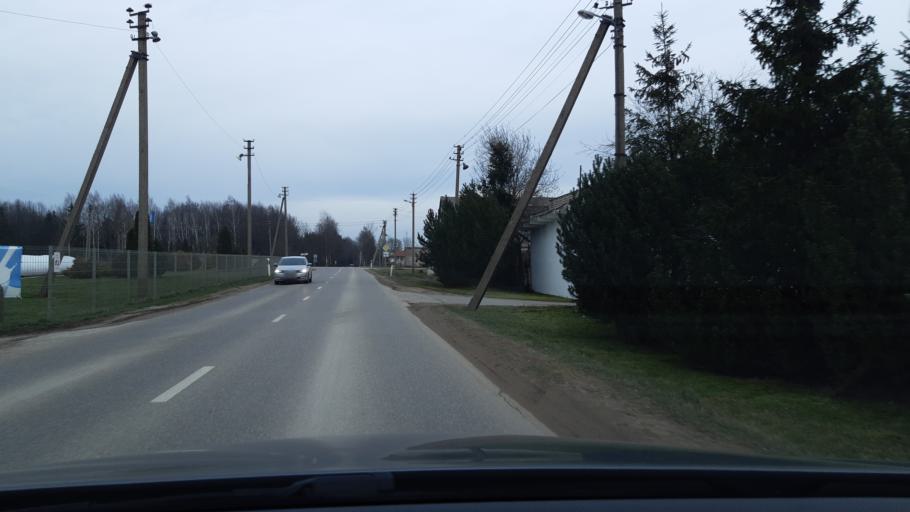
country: LT
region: Kauno apskritis
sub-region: Kaunas
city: Sargenai
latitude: 54.9552
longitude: 23.8596
